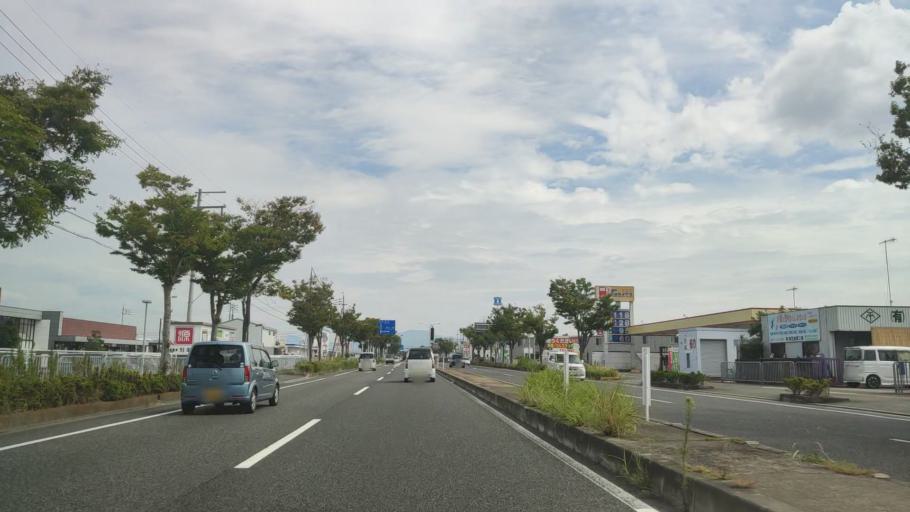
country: JP
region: Wakayama
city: Wakayama-shi
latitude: 34.2562
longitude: 135.2271
